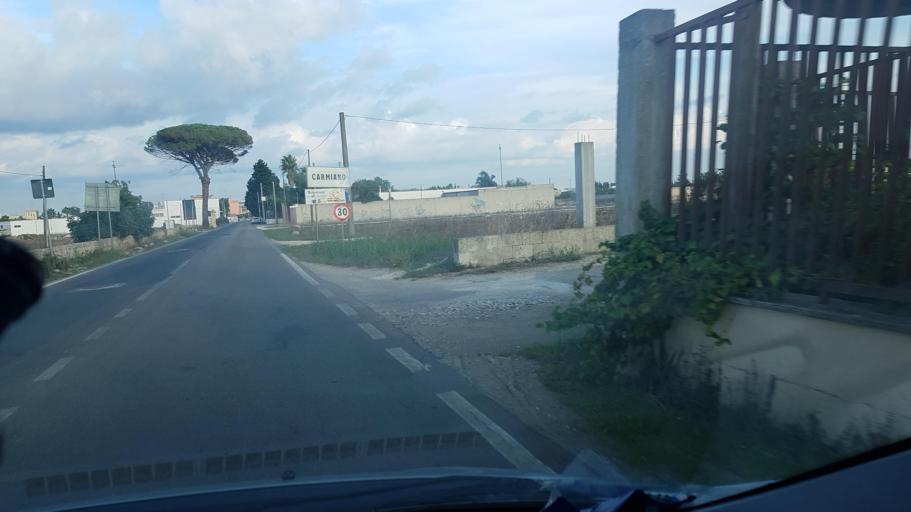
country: IT
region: Apulia
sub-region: Provincia di Lecce
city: Carmiano
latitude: 40.3457
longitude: 18.0294
